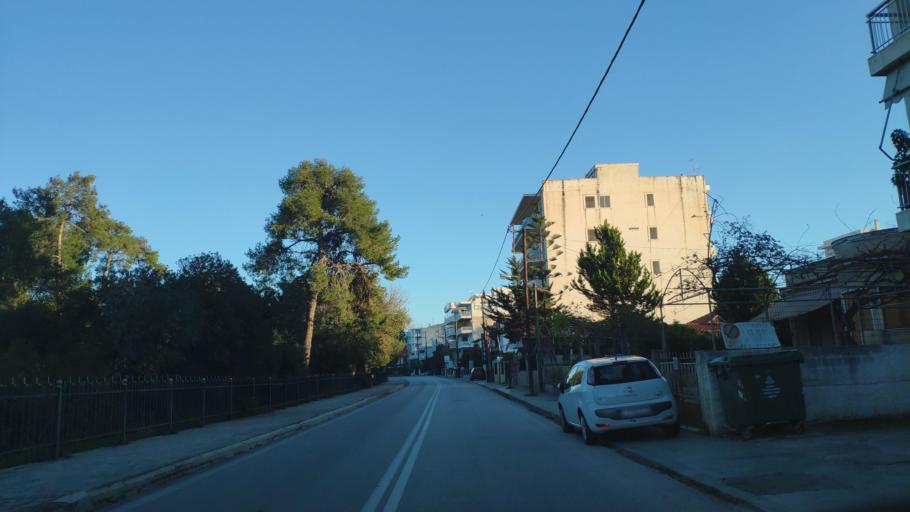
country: GR
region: Peloponnese
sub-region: Nomos Korinthias
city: Xylokastro
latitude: 38.0738
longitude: 22.6420
